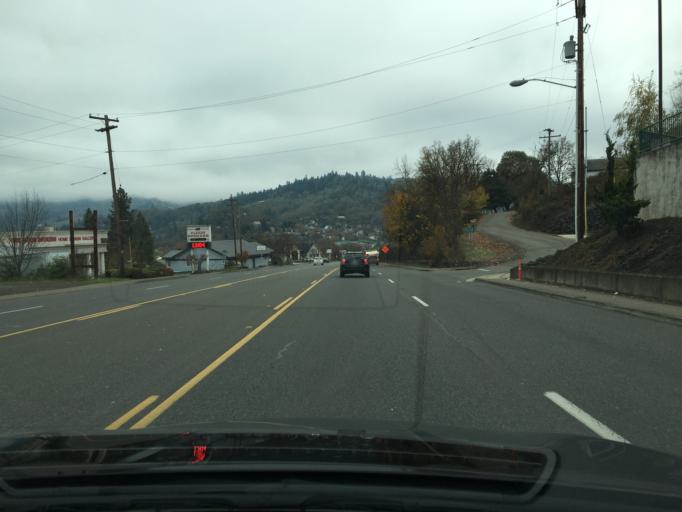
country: US
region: Oregon
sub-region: Douglas County
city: Roseburg
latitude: 43.2190
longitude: -123.3443
